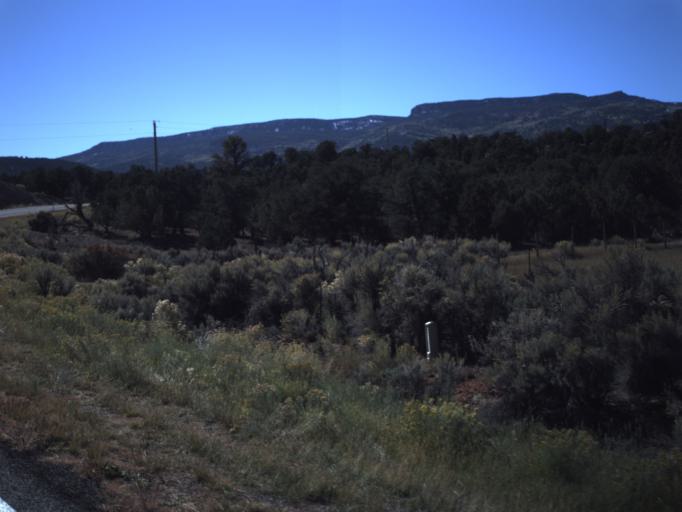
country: US
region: Utah
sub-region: Wayne County
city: Loa
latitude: 38.2222
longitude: -111.3428
